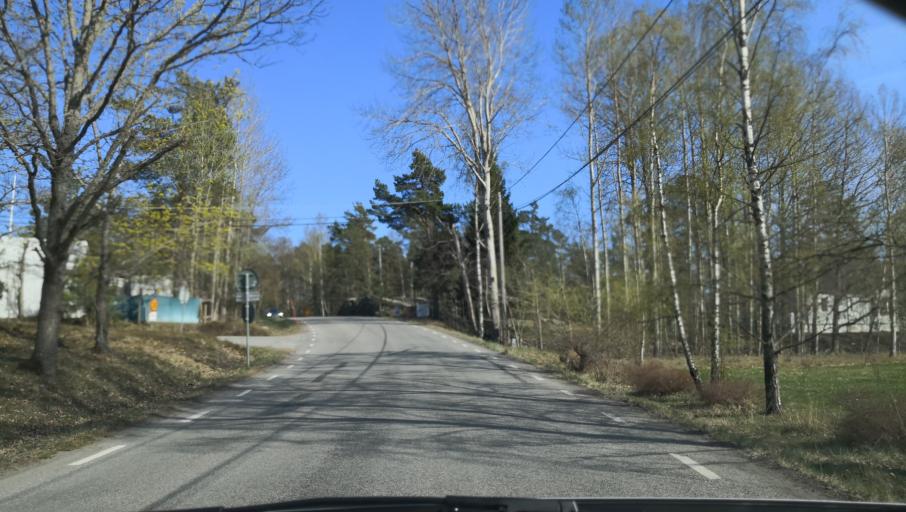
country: SE
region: Stockholm
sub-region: Varmdo Kommun
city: Holo
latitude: 59.3032
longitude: 18.6327
